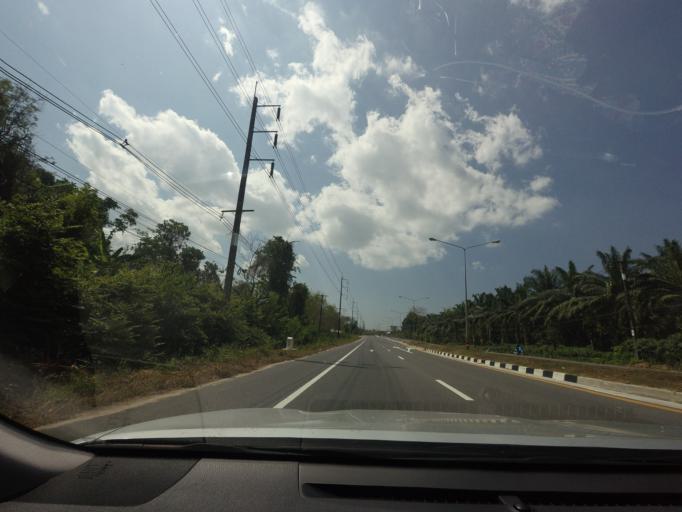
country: TH
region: Phangnga
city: Thai Mueang
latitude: 8.4756
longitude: 98.2663
